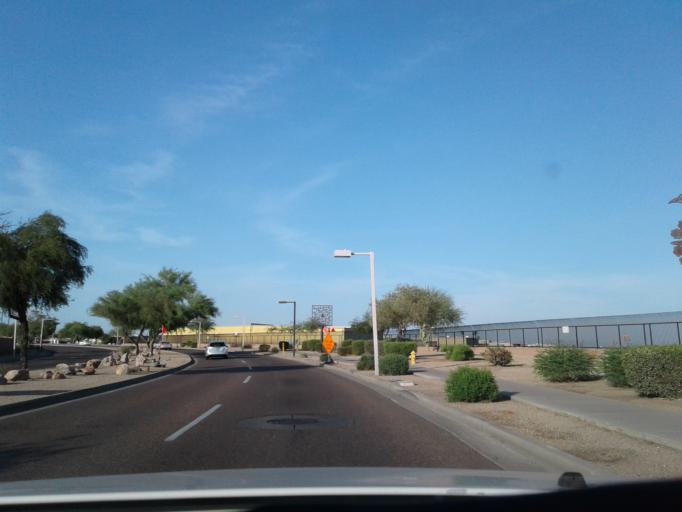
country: US
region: Arizona
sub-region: Maricopa County
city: Phoenix
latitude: 33.4423
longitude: -112.0323
